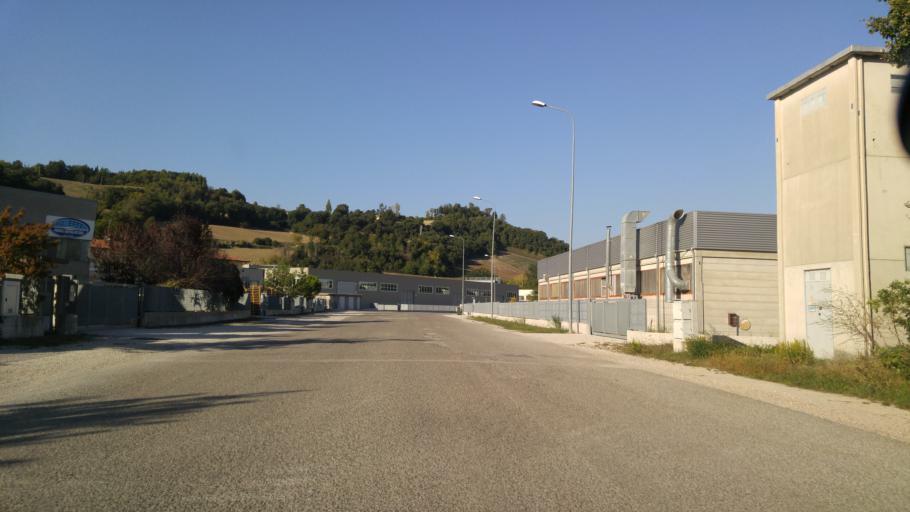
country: IT
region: The Marches
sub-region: Provincia di Pesaro e Urbino
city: Fermignano
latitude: 43.6925
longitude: 12.6489
